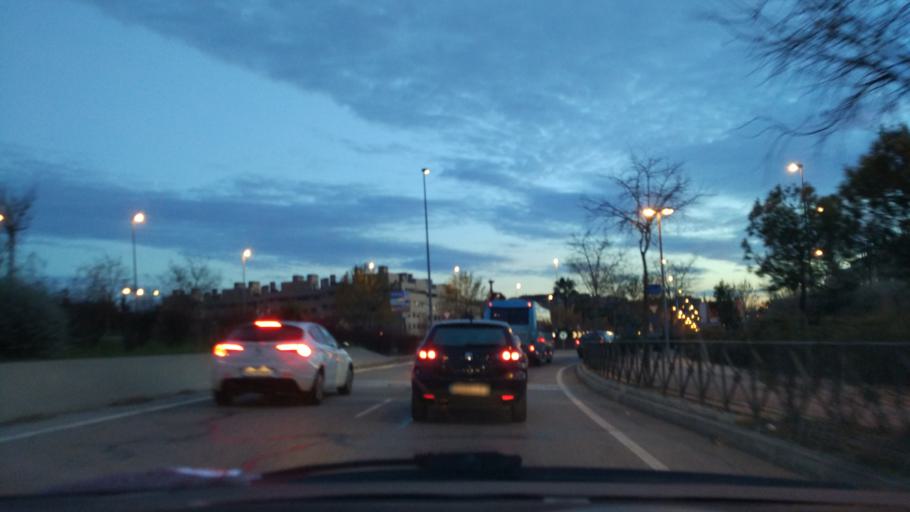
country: ES
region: Madrid
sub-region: Provincia de Madrid
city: Leganes
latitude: 40.3472
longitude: -3.7702
